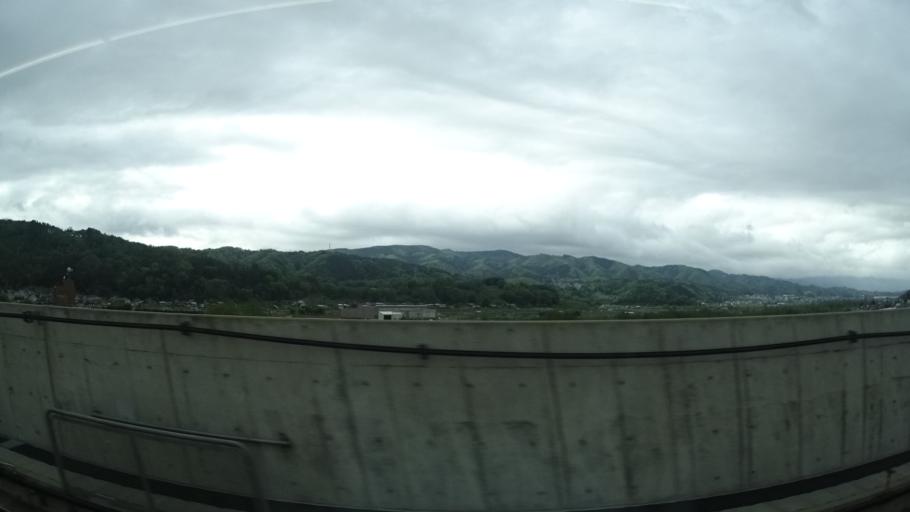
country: JP
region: Nagano
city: Nakano
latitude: 36.7903
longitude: 138.3603
